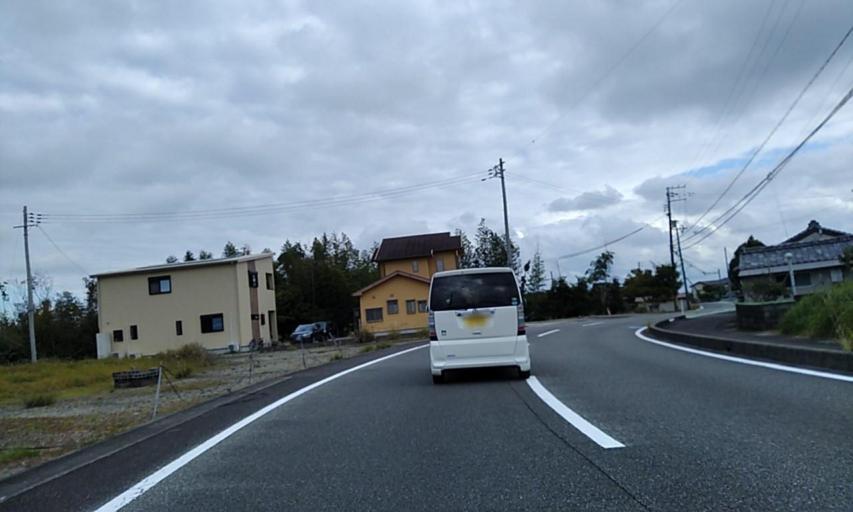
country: JP
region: Wakayama
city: Shingu
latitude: 33.5856
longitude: 135.9483
